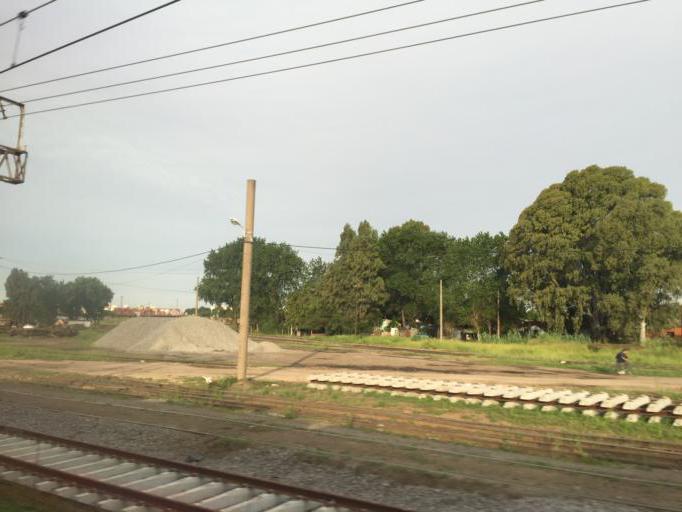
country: AR
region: Buenos Aires
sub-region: Partido de Avellaneda
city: Avellaneda
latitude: -34.6780
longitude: -58.3795
